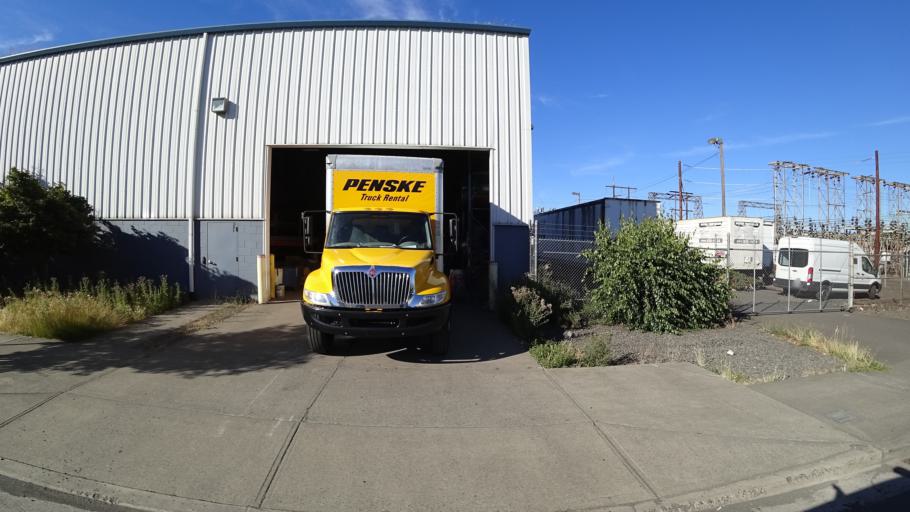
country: US
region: Oregon
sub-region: Multnomah County
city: Portland
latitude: 45.5388
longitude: -122.6790
